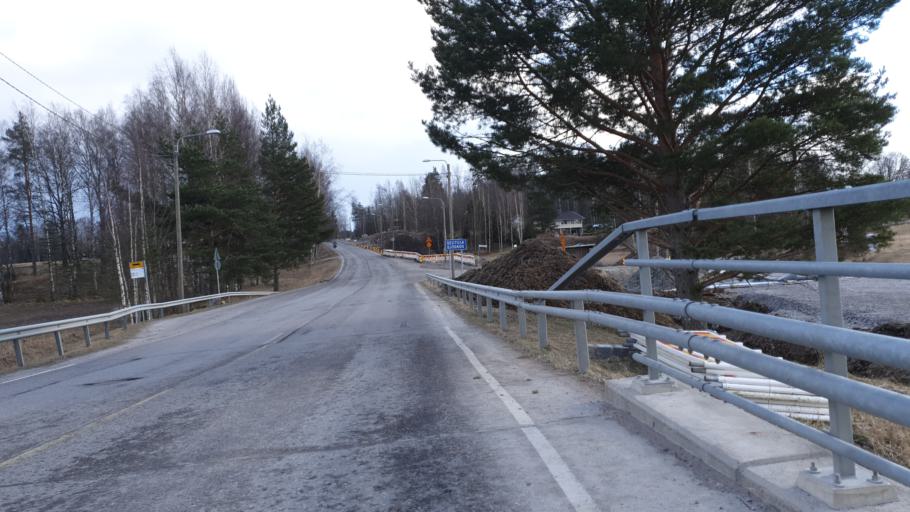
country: FI
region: Uusimaa
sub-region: Helsinki
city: Nurmijaervi
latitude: 60.3585
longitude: 24.8583
